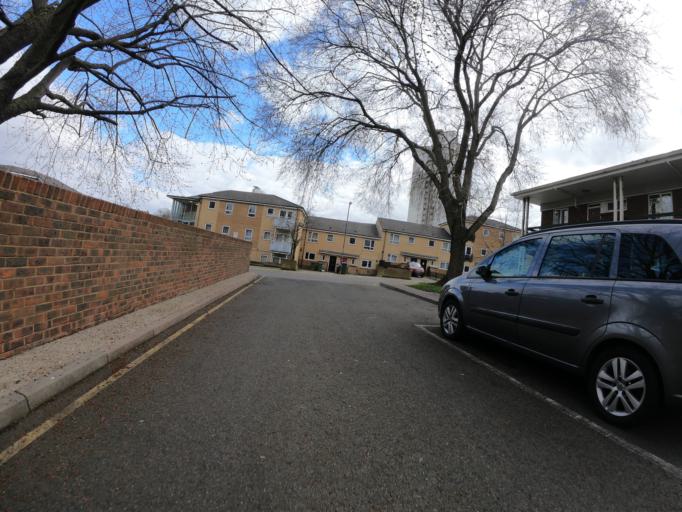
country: GB
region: England
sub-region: Greater London
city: Woolwich
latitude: 51.4900
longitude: 0.0573
